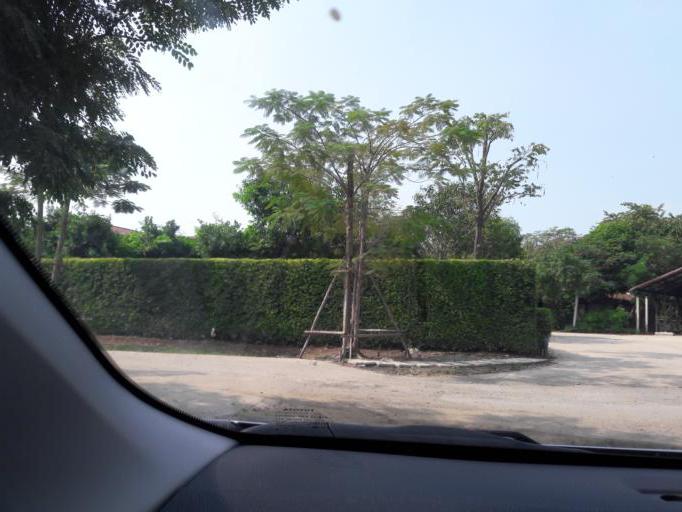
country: TH
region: Ang Thong
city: Ang Thong
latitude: 14.5411
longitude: 100.4326
